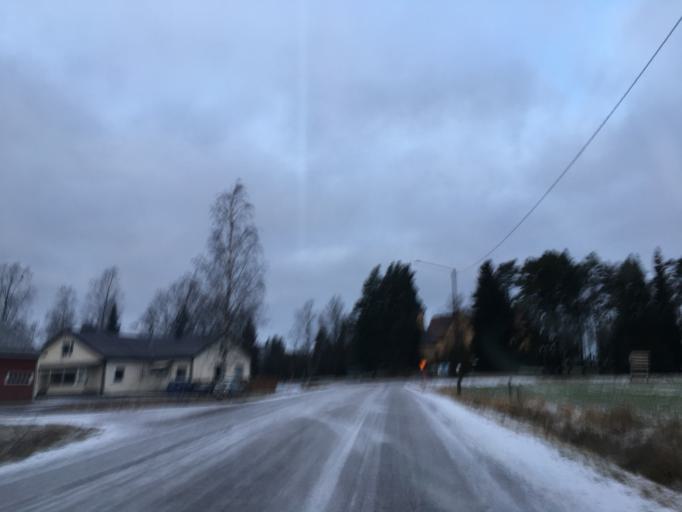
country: FI
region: Varsinais-Suomi
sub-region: Loimaa
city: Aura
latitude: 60.6078
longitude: 22.5644
